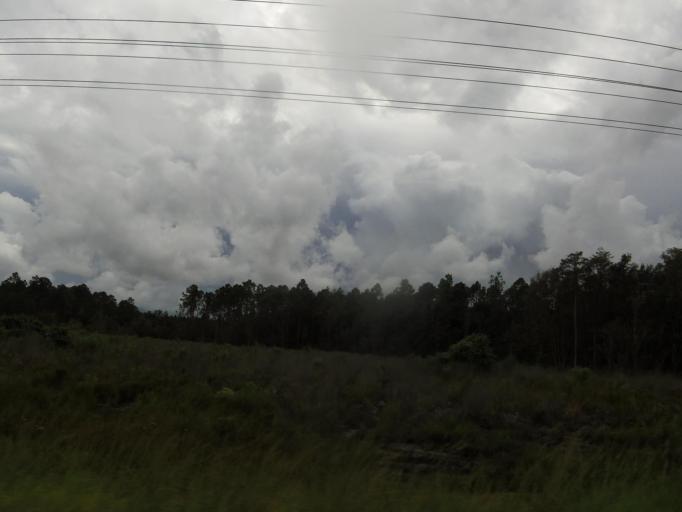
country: US
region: Florida
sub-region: Nassau County
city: Hilliard
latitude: 30.5219
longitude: -82.0696
